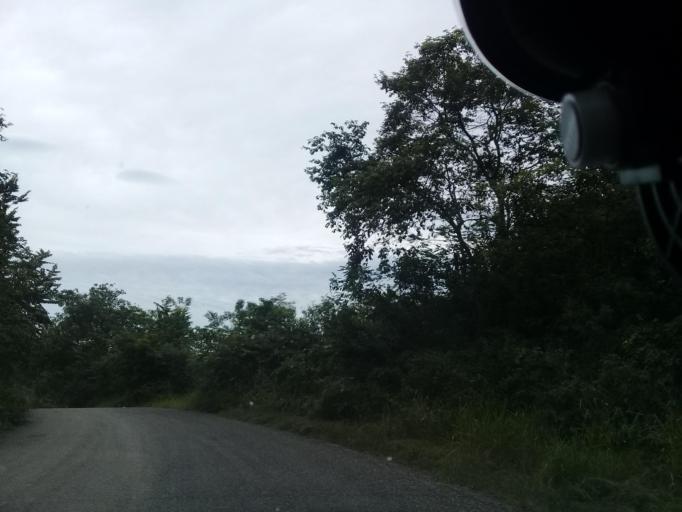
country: MX
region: Hidalgo
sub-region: Huejutla de Reyes
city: Chalahuiyapa
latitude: 21.2006
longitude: -98.3501
